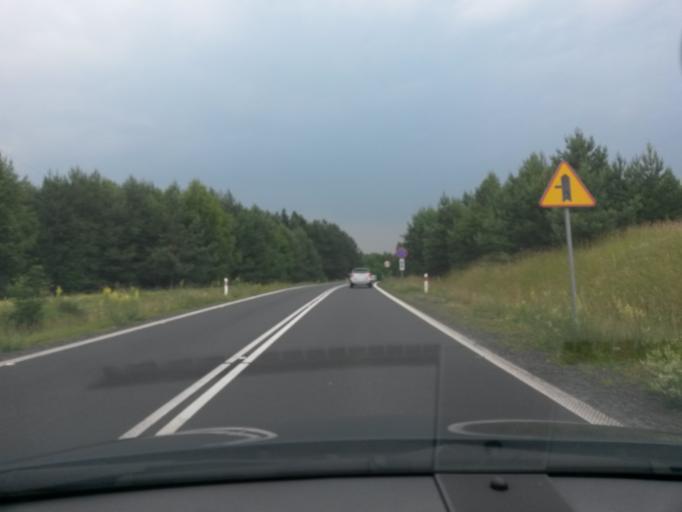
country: PL
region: Silesian Voivodeship
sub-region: Powiat czestochowski
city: Olsztyn
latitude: 50.7602
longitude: 19.2334
